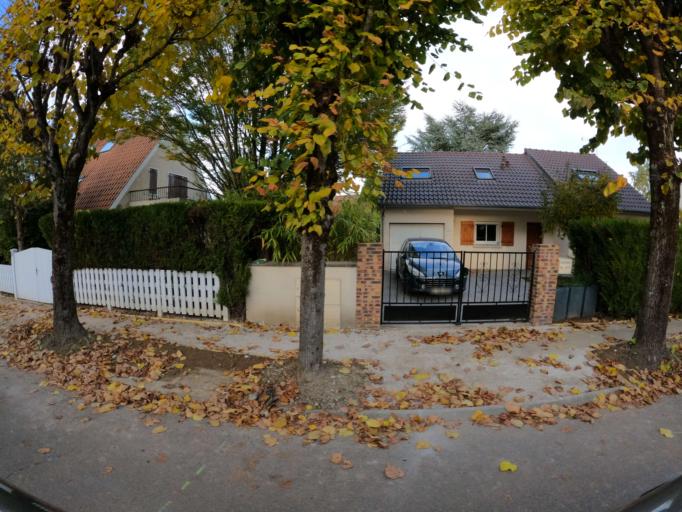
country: FR
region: Ile-de-France
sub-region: Departement de Seine-et-Marne
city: Pontault-Combault
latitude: 48.8023
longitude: 2.5992
